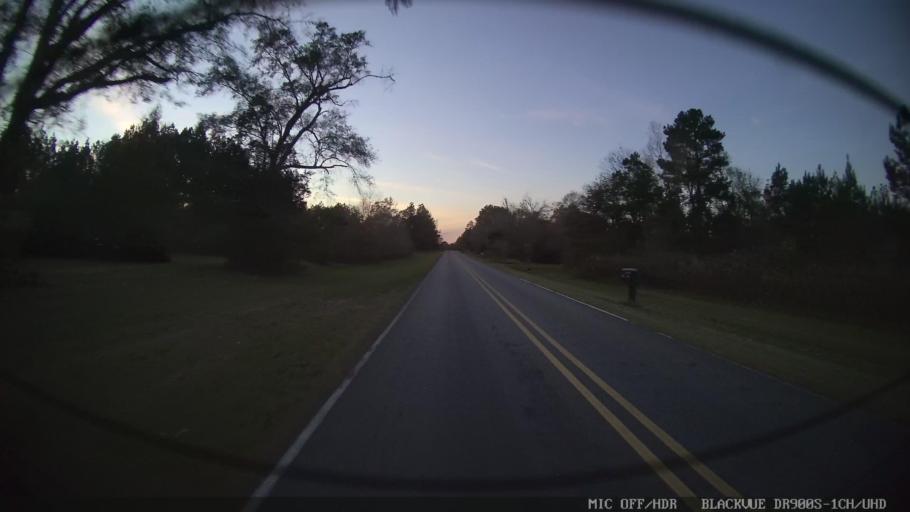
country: US
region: Mississippi
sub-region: Perry County
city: New Augusta
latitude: 31.0715
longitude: -89.2008
